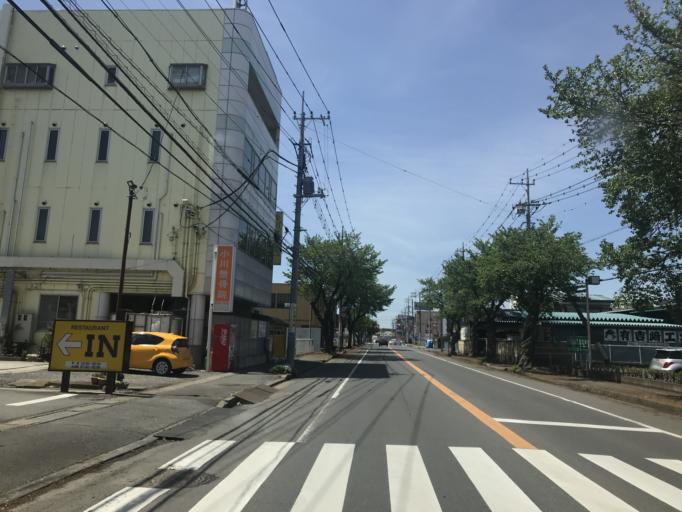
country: JP
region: Ibaraki
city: Shimodate
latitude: 36.3010
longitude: 139.9804
